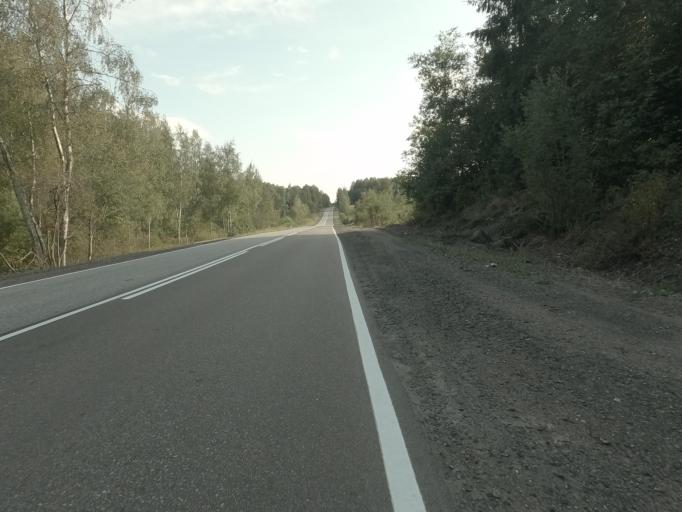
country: RU
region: Leningrad
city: Vyborg
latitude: 60.8399
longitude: 28.8404
